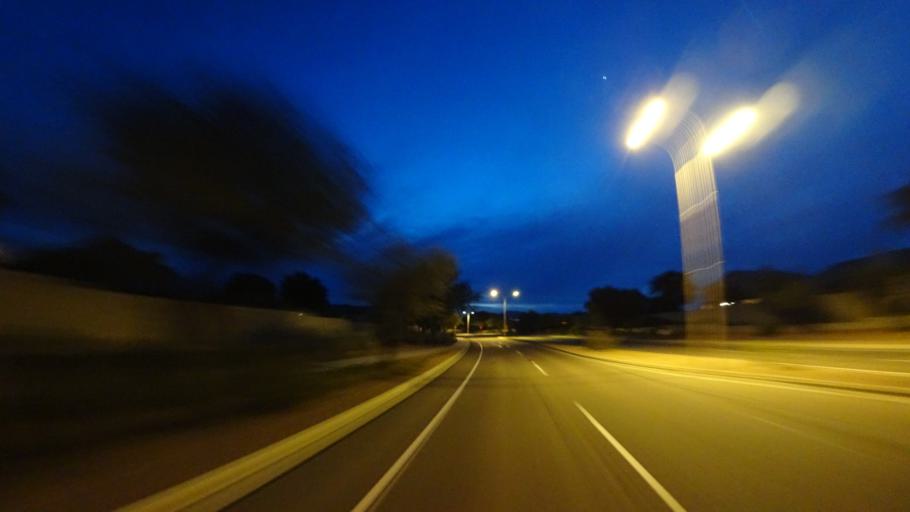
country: US
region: Arizona
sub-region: Maricopa County
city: Guadalupe
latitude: 33.3116
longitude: -112.0259
